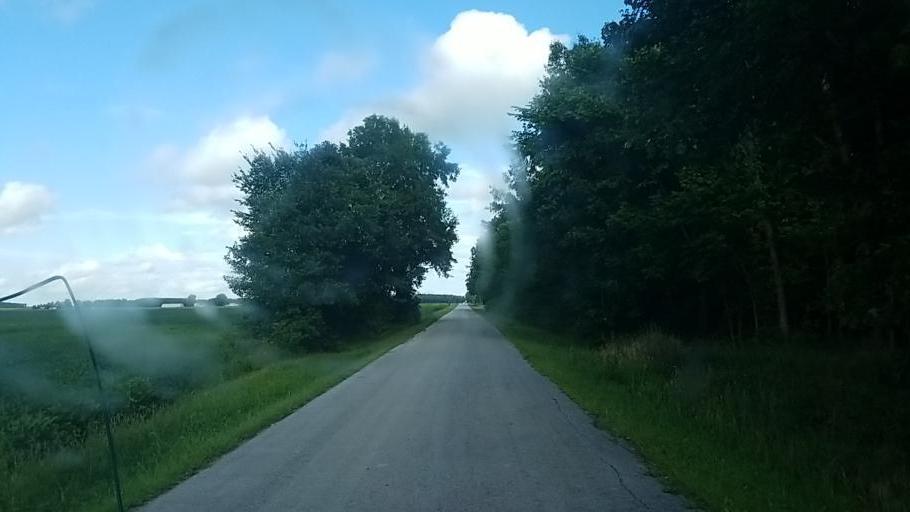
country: US
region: Ohio
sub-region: Hardin County
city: Forest
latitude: 40.7597
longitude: -83.4909
